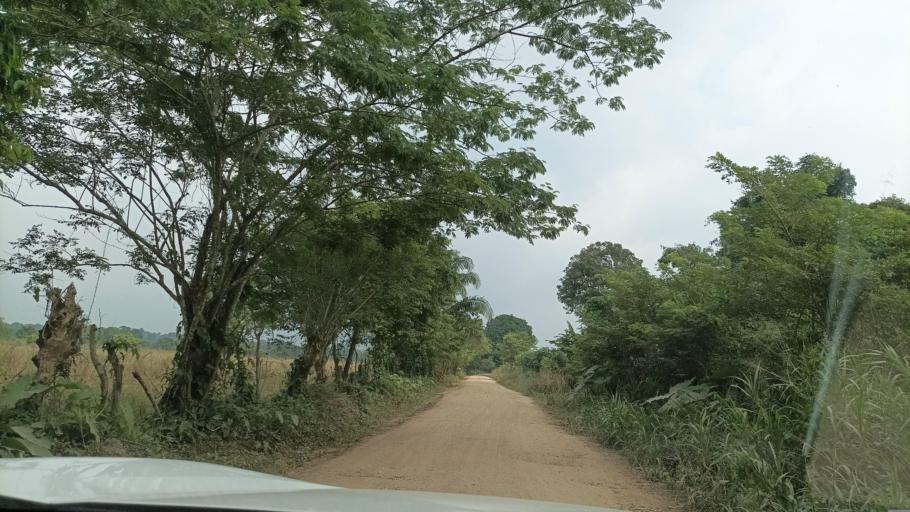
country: MX
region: Veracruz
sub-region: Moloacan
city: Cuichapa
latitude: 17.5819
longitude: -94.2207
